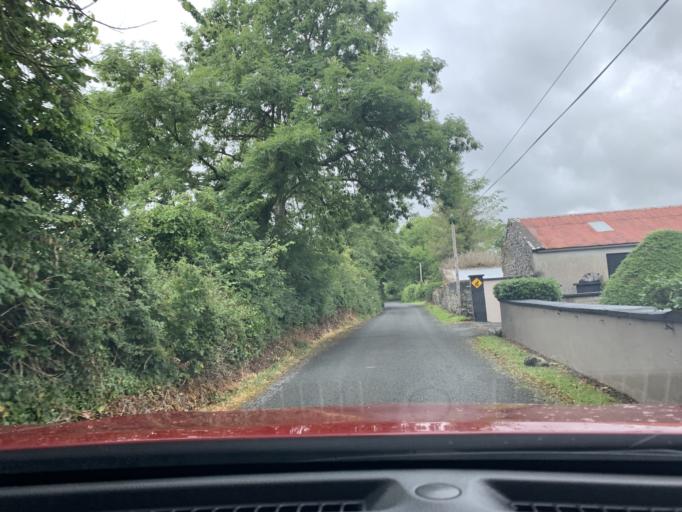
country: IE
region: Connaught
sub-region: Sligo
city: Sligo
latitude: 54.3021
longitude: -8.4573
